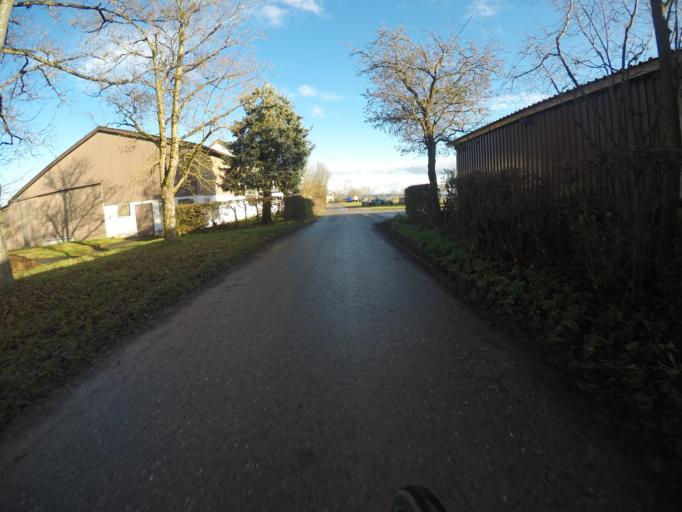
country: DE
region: Baden-Wuerttemberg
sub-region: Regierungsbezirk Stuttgart
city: Herrenberg
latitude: 48.5608
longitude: 8.8616
